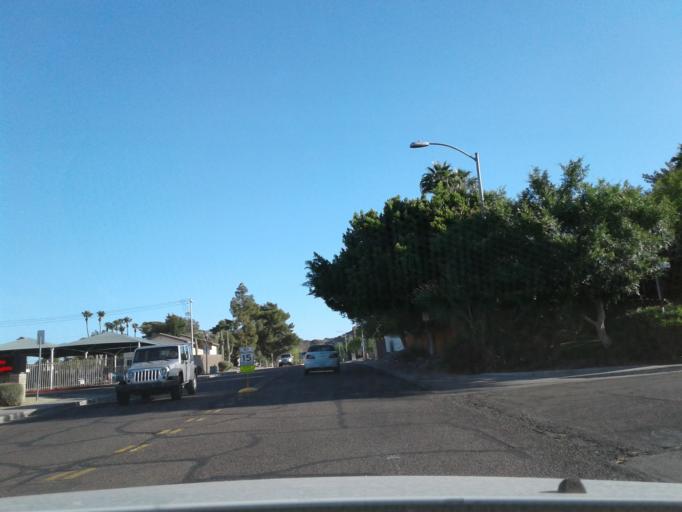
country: US
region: Arizona
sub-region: Maricopa County
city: Paradise Valley
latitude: 33.5410
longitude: -112.0346
